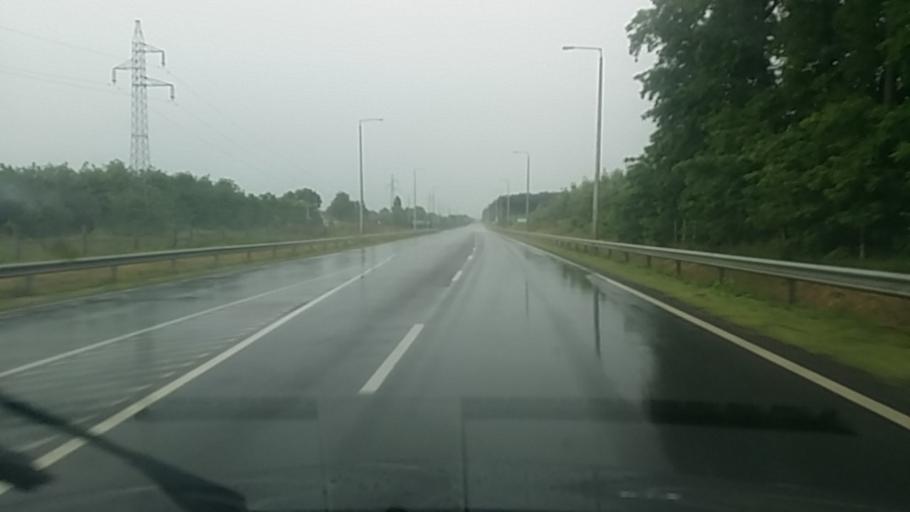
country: HU
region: Hajdu-Bihar
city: Hajduhadhaz
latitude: 47.6509
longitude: 21.6500
